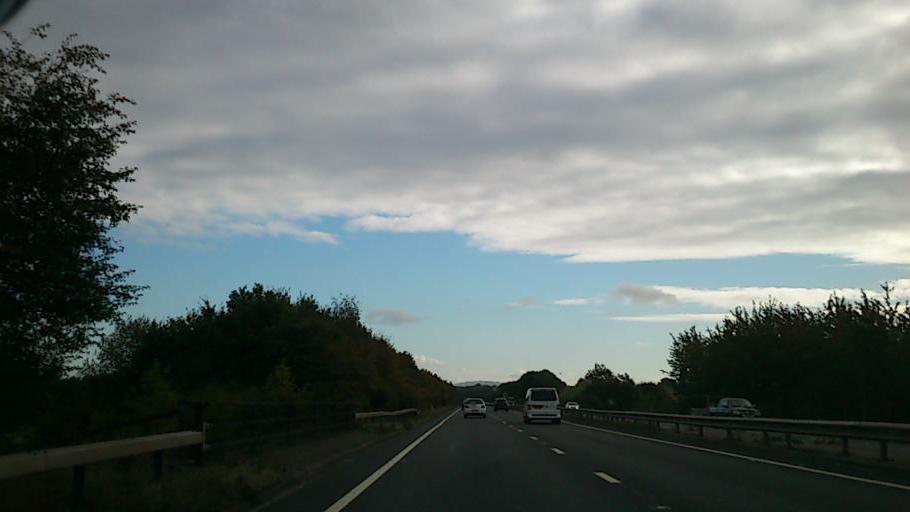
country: GB
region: England
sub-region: Shropshire
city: Bayston Hill
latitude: 52.6832
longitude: -2.7810
